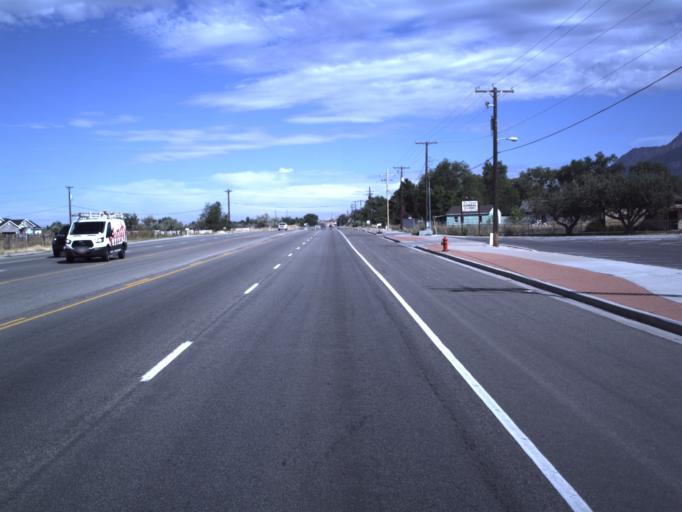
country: US
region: Utah
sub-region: Weber County
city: Harrisville
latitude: 41.2831
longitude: -111.9868
